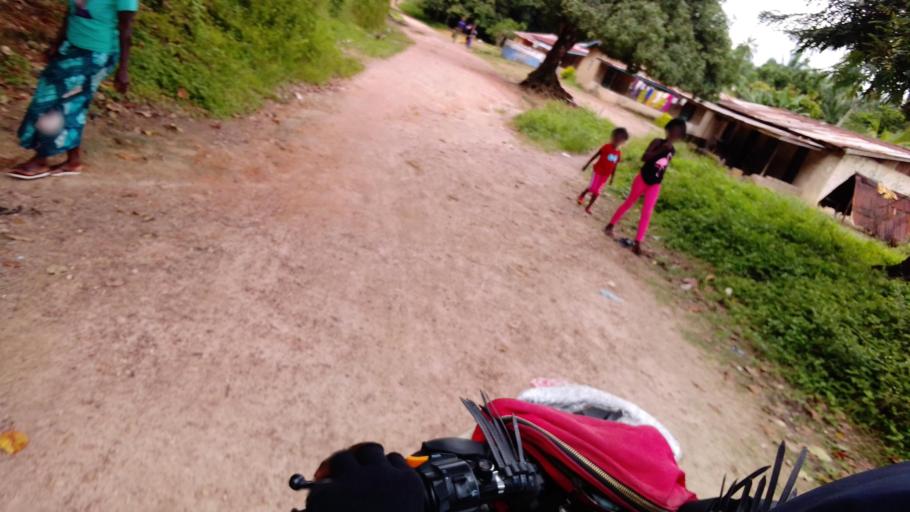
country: SL
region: Eastern Province
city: Koidu
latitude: 8.6751
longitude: -10.9790
